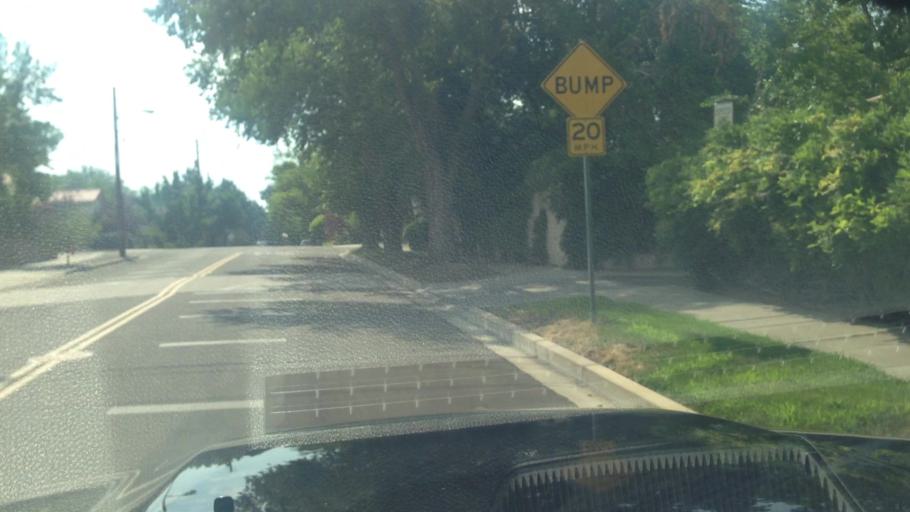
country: US
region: Nevada
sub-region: Washoe County
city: Reno
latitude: 39.5148
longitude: -119.8218
